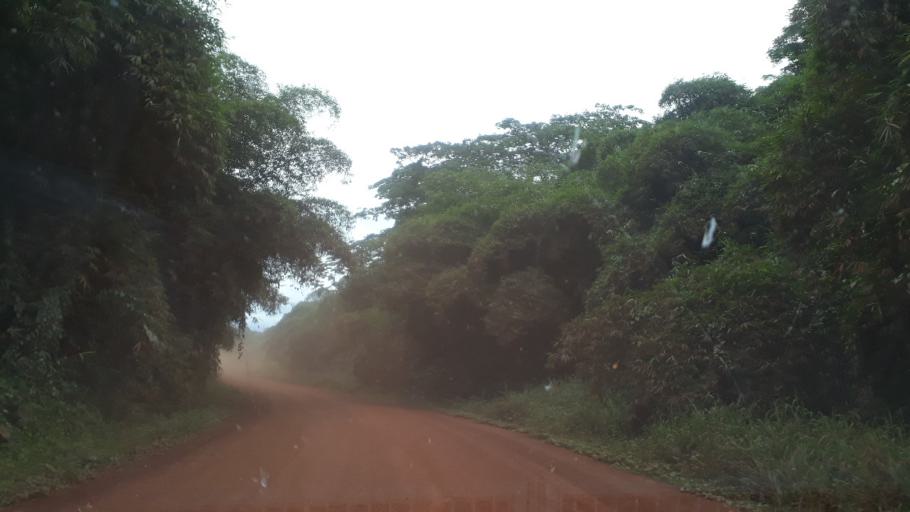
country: CD
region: Eastern Province
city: Kisangani
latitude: 0.5642
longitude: 25.8633
